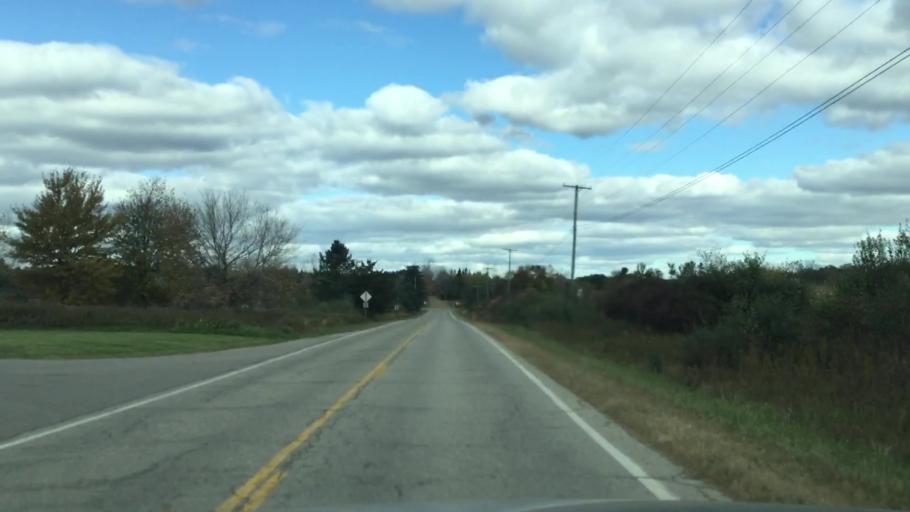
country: US
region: Michigan
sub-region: Lapeer County
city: Lapeer
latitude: 43.0691
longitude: -83.3311
